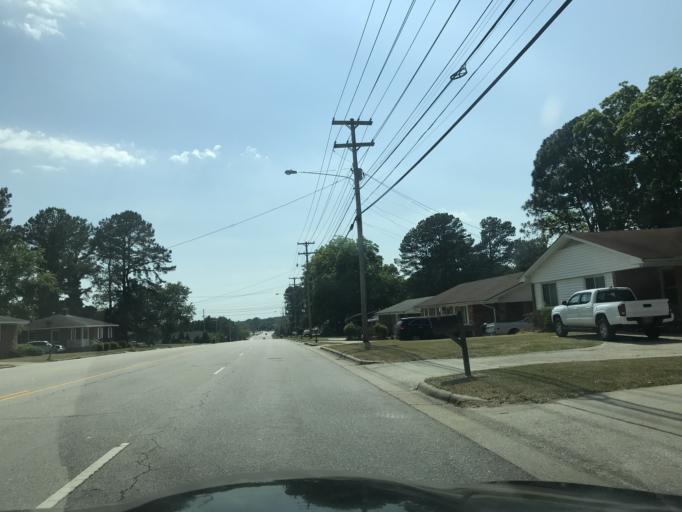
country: US
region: North Carolina
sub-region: Wilson County
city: Wilson
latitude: 35.7107
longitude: -77.9415
